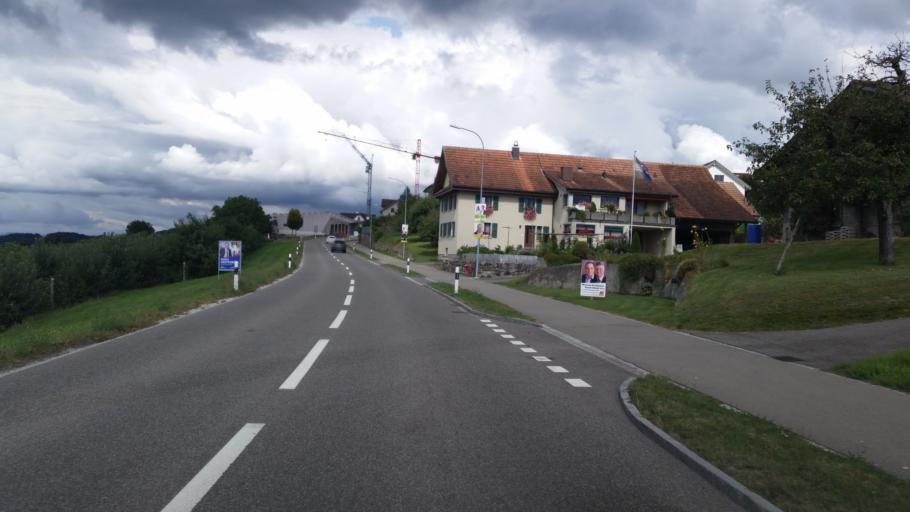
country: CH
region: Aargau
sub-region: Bezirk Bremgarten
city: Oberlunkhofen
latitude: 47.3082
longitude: 8.3906
